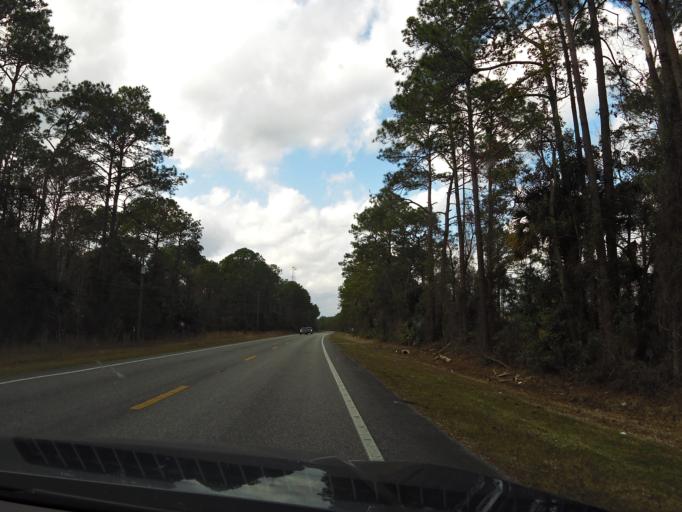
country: US
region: Florida
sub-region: Volusia County
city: Pierson
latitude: 29.1935
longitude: -81.4287
